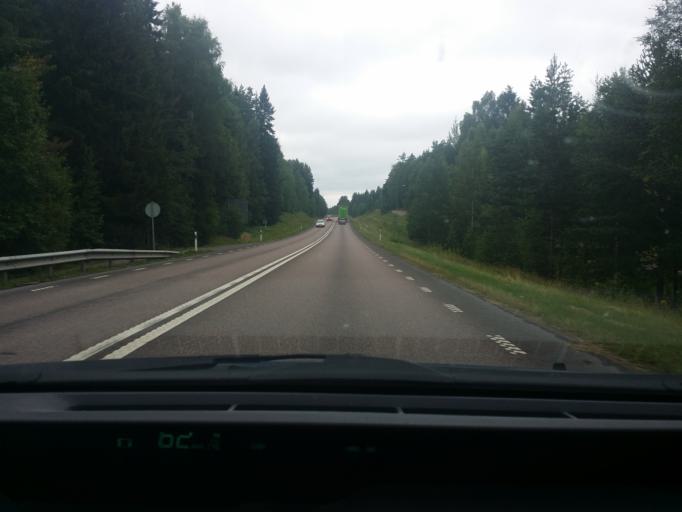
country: SE
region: Dalarna
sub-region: Borlange Kommun
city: Borlaenge
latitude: 60.5071
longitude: 15.3862
